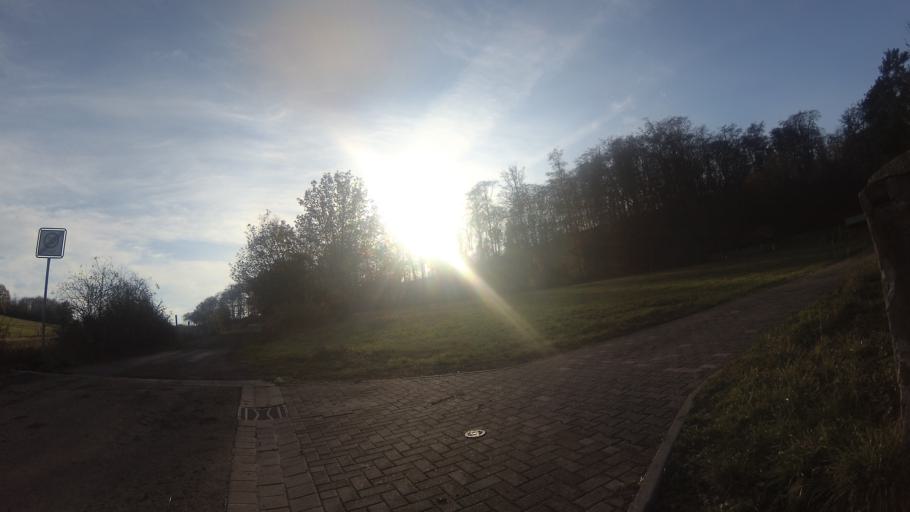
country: DE
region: Rheinland-Pfalz
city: Hahnweiler
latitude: 49.5487
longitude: 7.2038
